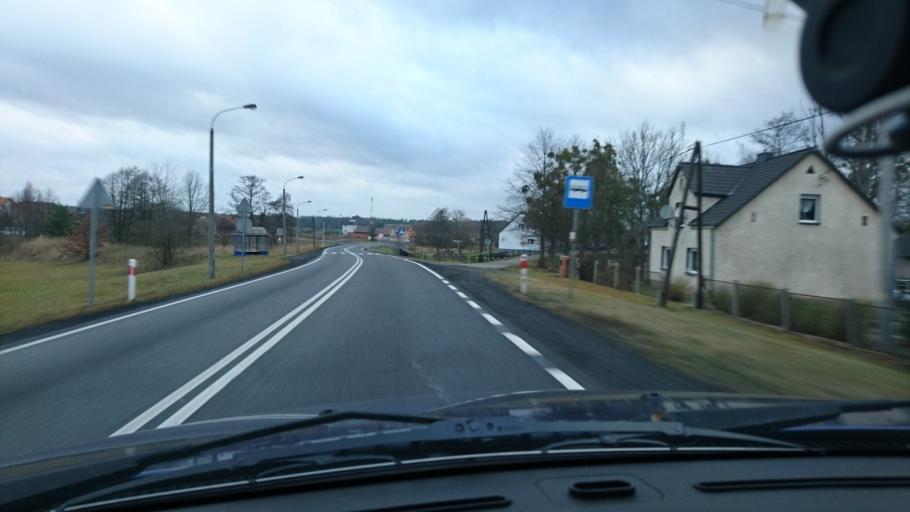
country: PL
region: Opole Voivodeship
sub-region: Powiat oleski
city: Olesno
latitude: 50.9120
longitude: 18.3527
